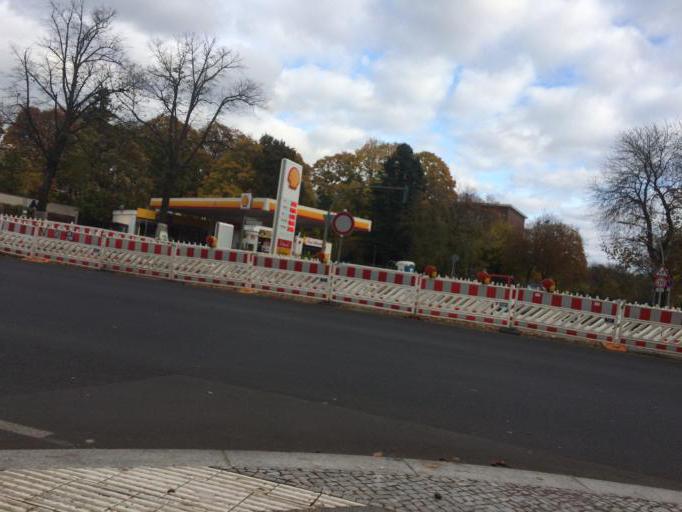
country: DE
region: Berlin
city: Wittenau
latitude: 52.5896
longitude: 13.3340
